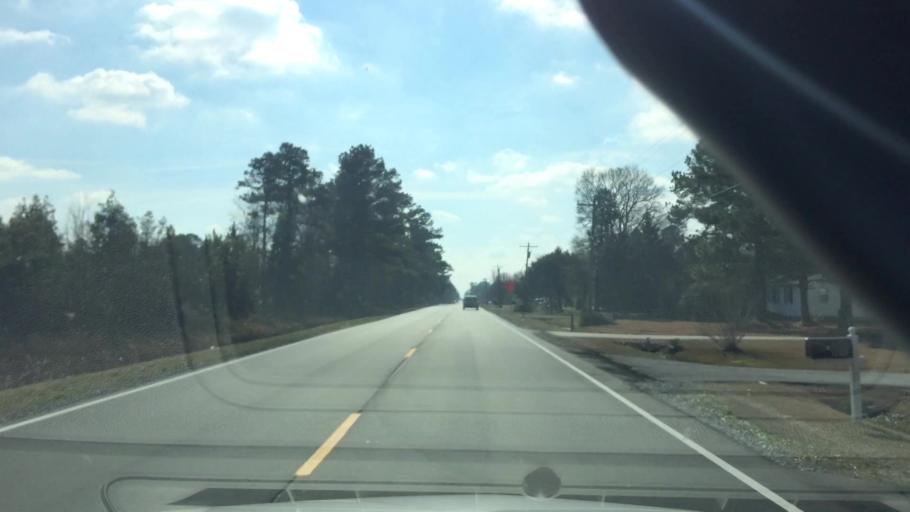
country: US
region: North Carolina
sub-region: Duplin County
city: Beulaville
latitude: 34.9943
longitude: -77.7566
